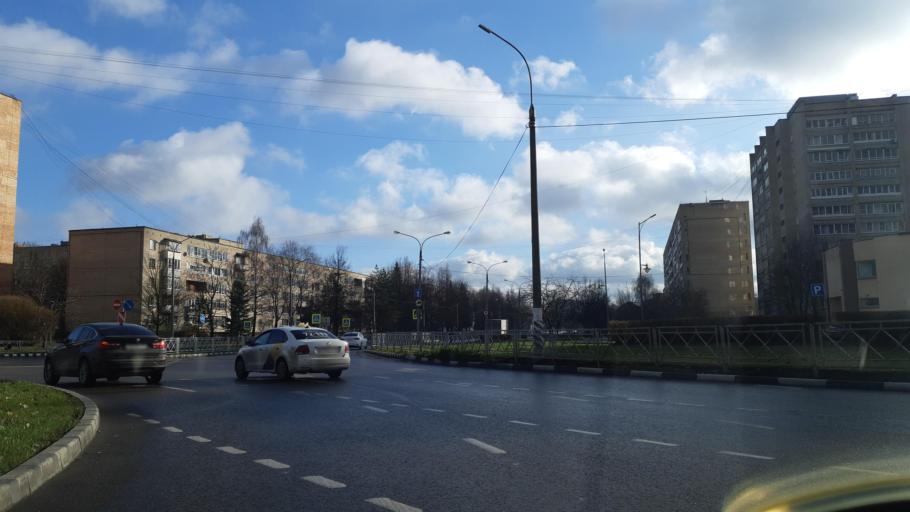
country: RU
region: Kaluga
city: Obninsk
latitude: 55.1169
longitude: 36.5967
